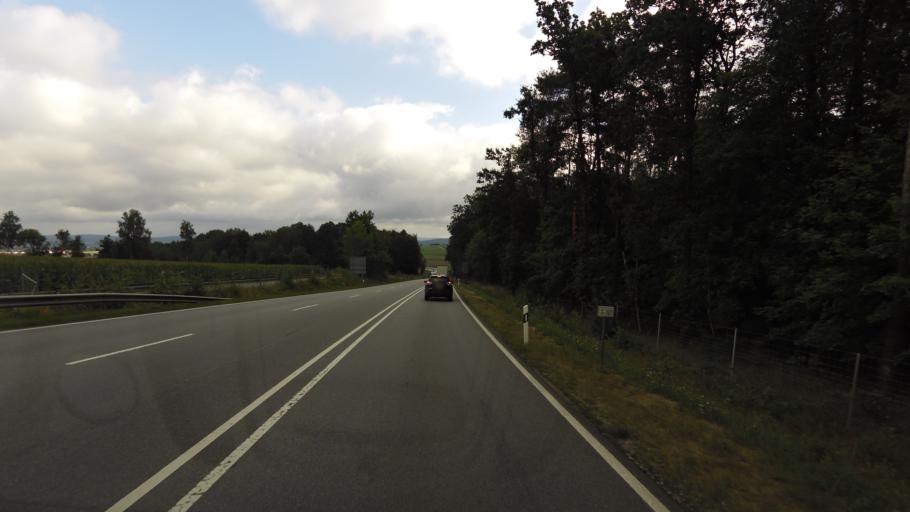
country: DE
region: Bavaria
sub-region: Upper Palatinate
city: Traitsching
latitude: 49.1795
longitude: 12.6499
